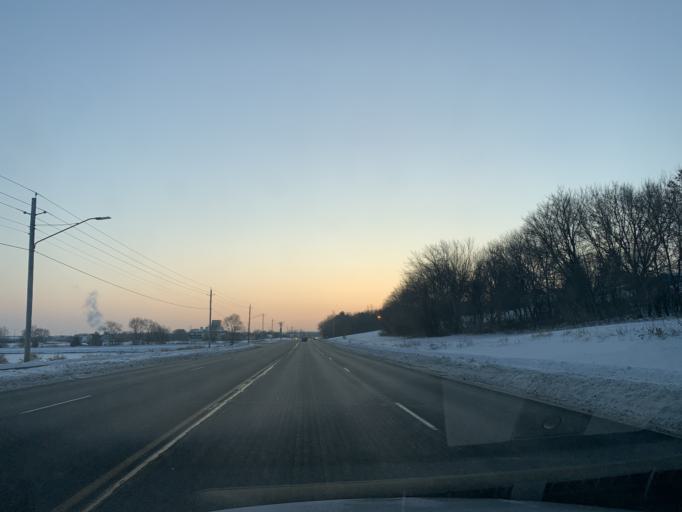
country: US
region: Minnesota
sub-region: Scott County
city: Shakopee
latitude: 44.7857
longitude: -93.4879
